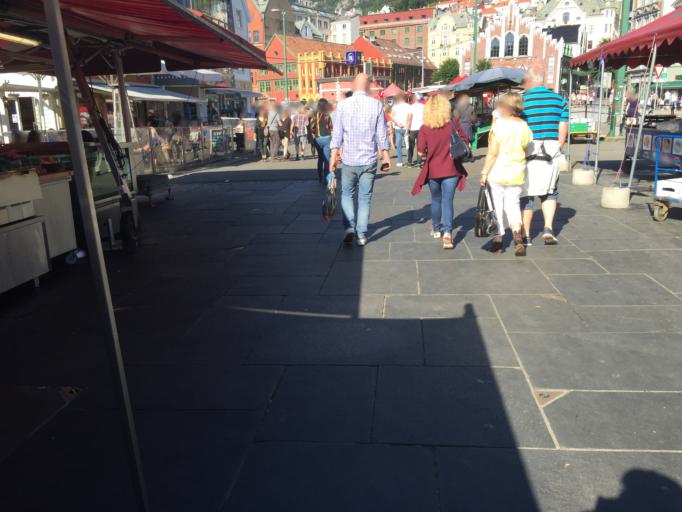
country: NO
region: Hordaland
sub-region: Bergen
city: Bergen
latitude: 60.3949
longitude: 5.3253
